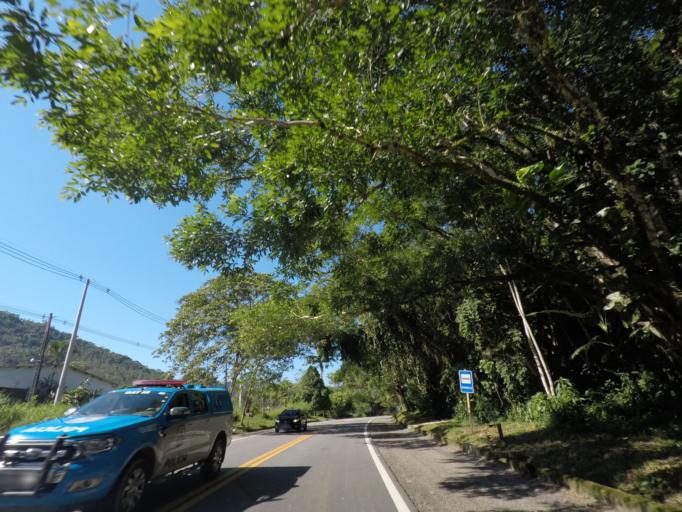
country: BR
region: Rio de Janeiro
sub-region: Parati
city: Paraty
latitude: -23.2916
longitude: -44.6974
